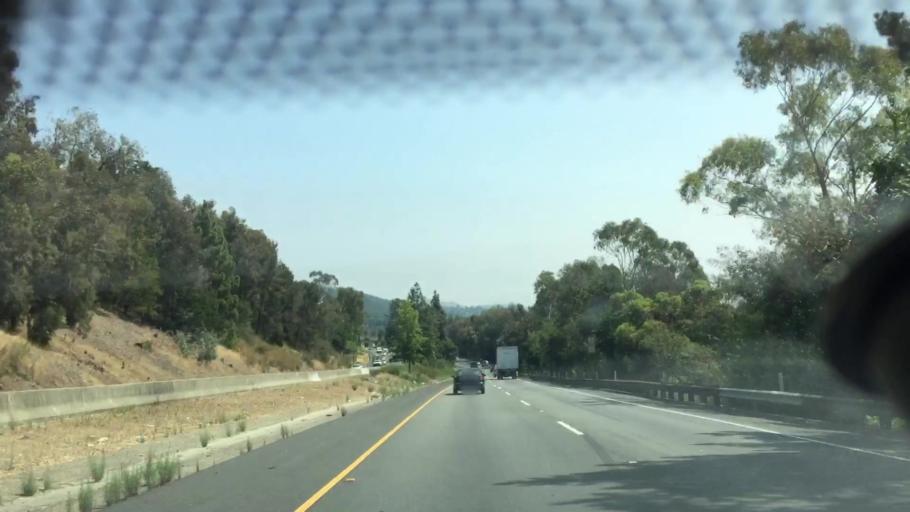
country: US
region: California
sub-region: Alameda County
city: Piedmont
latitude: 37.8052
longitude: -122.1921
